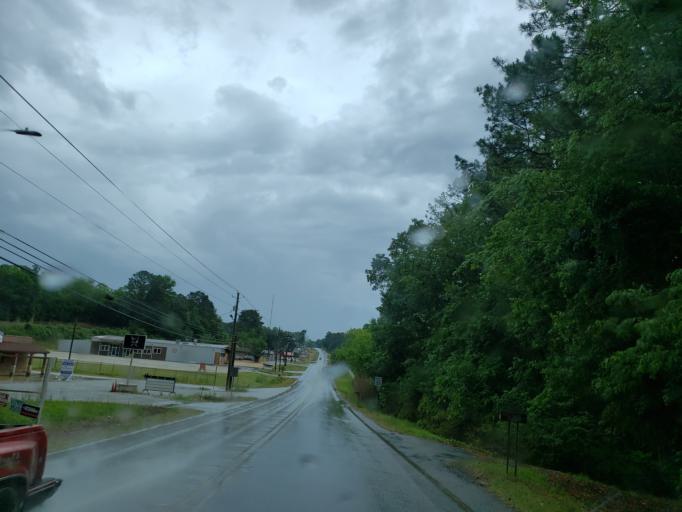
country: US
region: Georgia
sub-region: Haralson County
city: Buchanan
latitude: 33.7982
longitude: -85.1892
